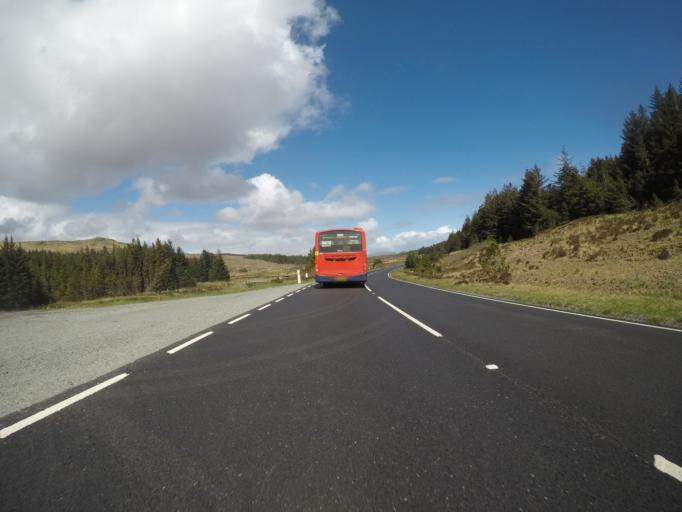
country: GB
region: Scotland
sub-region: Highland
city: Isle of Skye
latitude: 57.3288
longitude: -6.2030
